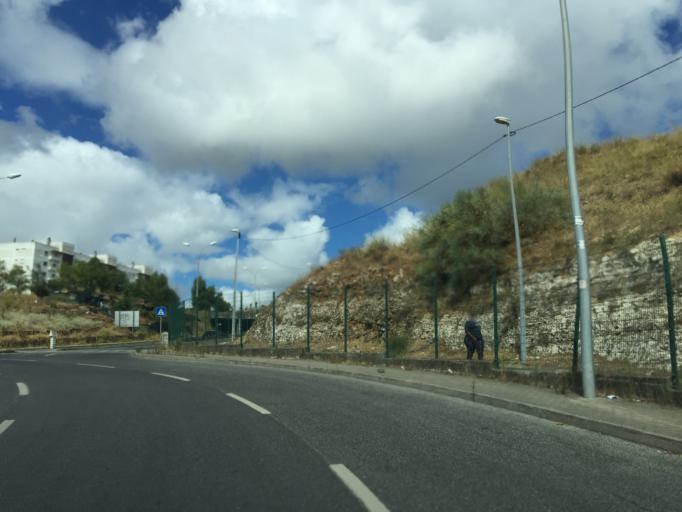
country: PT
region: Lisbon
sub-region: Amadora
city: Amadora
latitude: 38.7720
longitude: -9.2251
